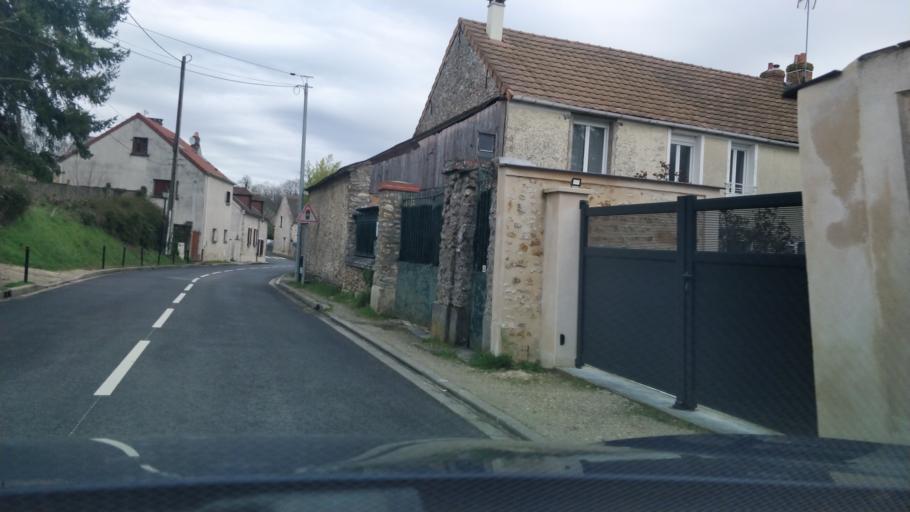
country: FR
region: Ile-de-France
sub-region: Departement de l'Essonne
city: Vaugrigneuse
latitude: 48.6016
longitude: 2.1206
